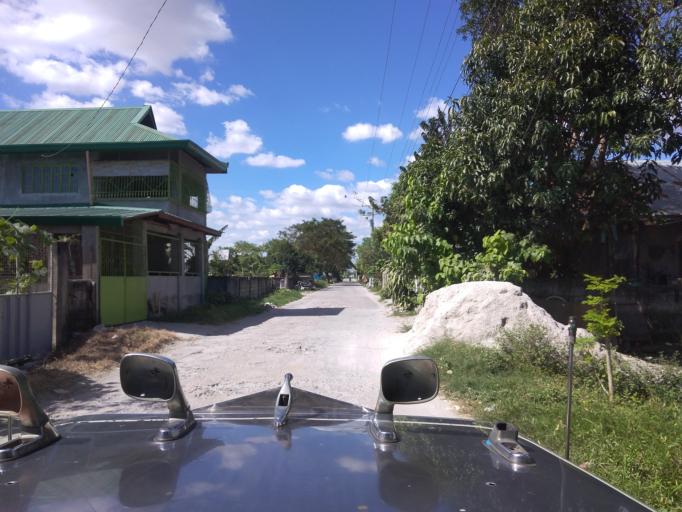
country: PH
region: Central Luzon
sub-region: Province of Pampanga
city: Bacolor
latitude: 15.0137
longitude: 120.6428
